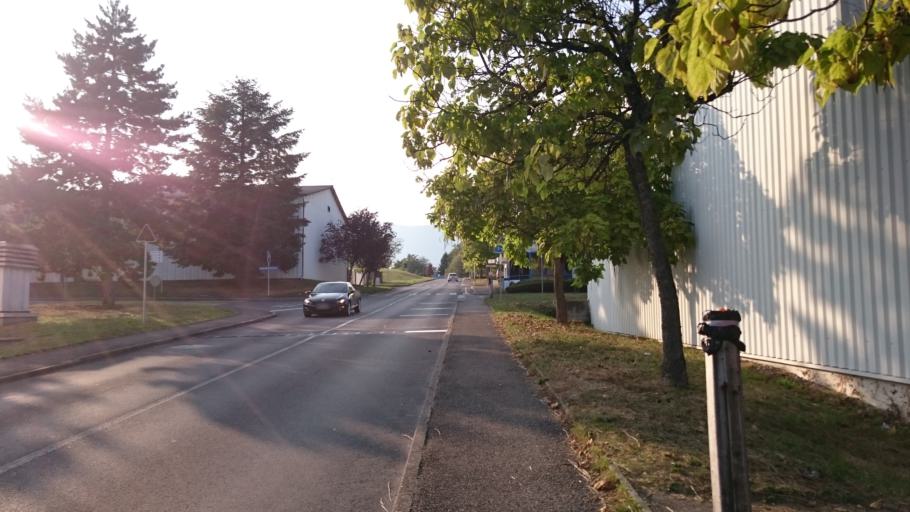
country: CH
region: Geneva
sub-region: Geneva
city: Satigny
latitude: 46.2344
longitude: 6.0486
